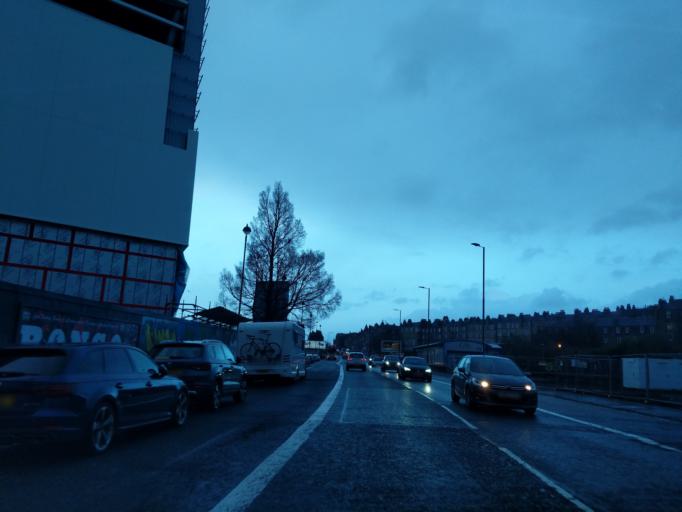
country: GB
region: Scotland
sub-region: West Lothian
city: Seafield
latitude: 55.9561
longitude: -3.1597
